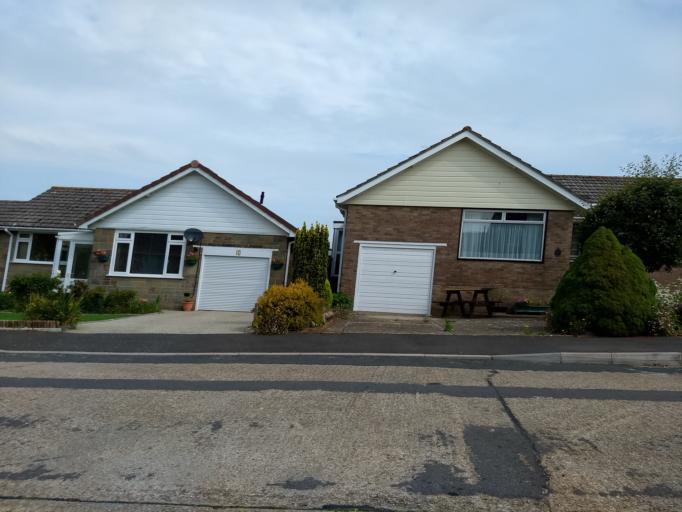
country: GB
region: England
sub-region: Isle of Wight
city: Ryde
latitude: 50.7217
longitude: -1.1803
